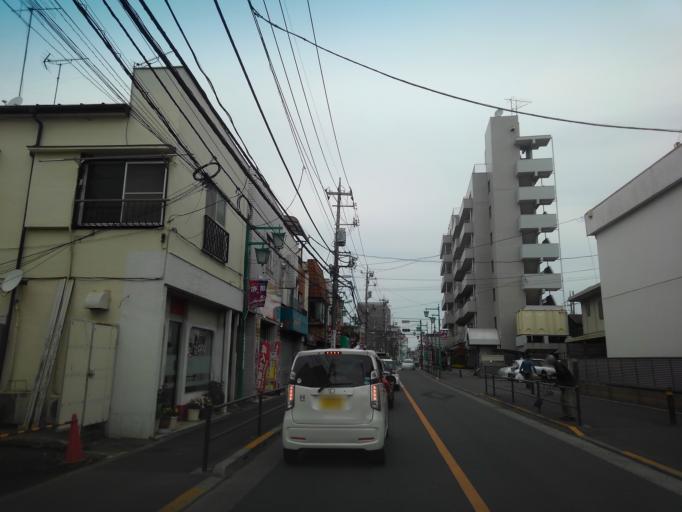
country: JP
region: Tokyo
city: Chofugaoka
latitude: 35.6505
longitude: 139.5510
